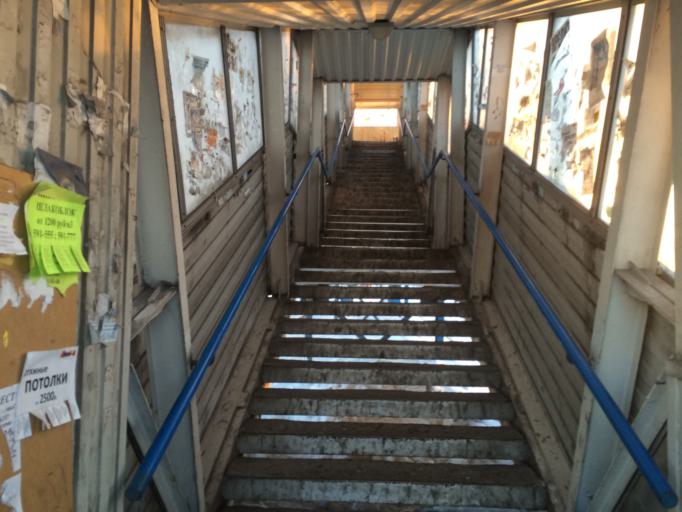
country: RU
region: Chelyabinsk
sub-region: Gorod Magnitogorsk
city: Magnitogorsk
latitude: 53.4022
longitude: 59.0262
